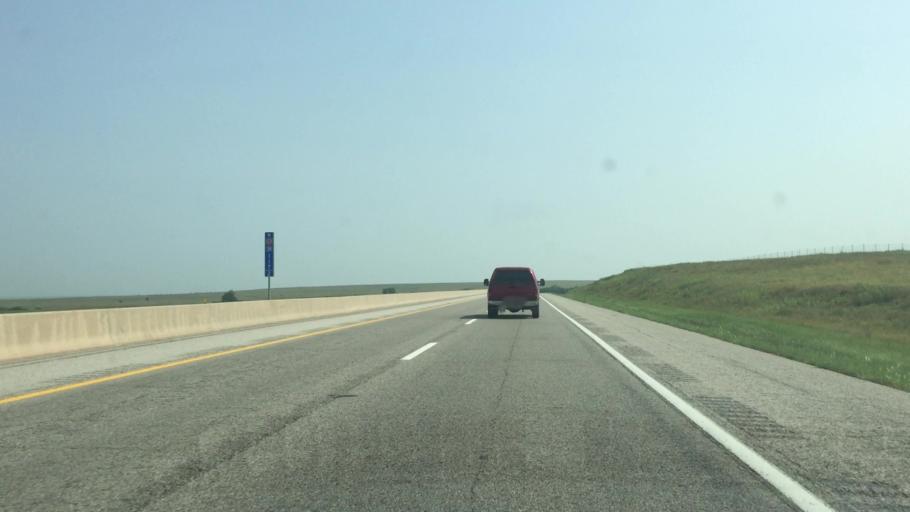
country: US
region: Kansas
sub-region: Lyon County
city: Emporia
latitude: 38.3048
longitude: -96.3458
